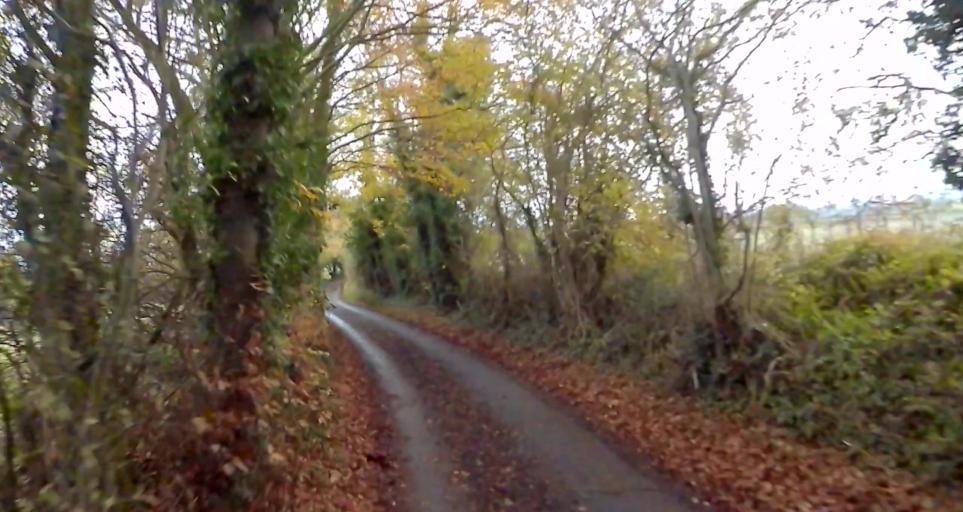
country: GB
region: England
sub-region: Hampshire
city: Odiham
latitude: 51.2423
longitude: -0.9080
